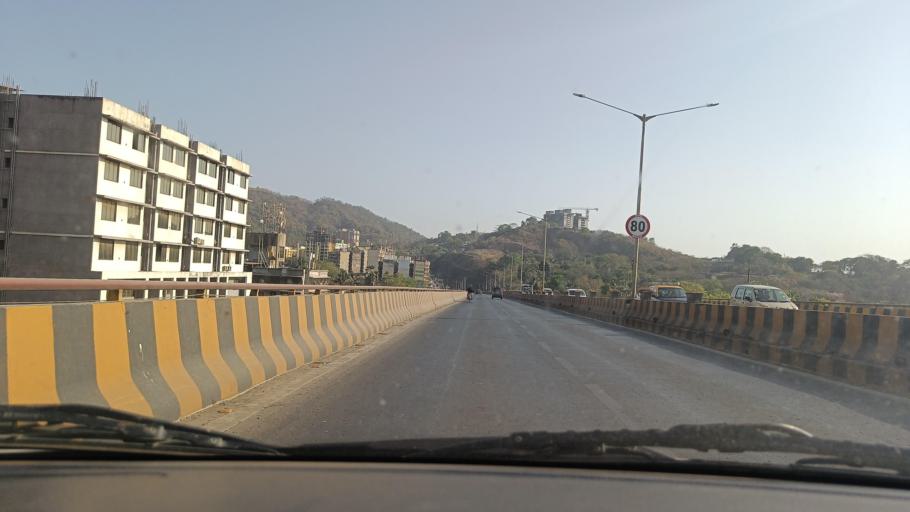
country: IN
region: Maharashtra
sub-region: Mumbai Suburban
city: Mumbai
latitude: 19.0452
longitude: 72.9091
